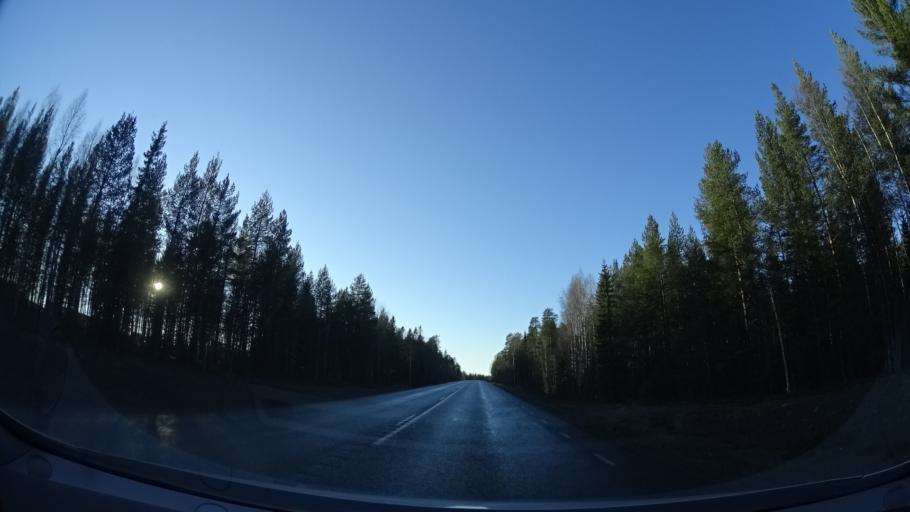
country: SE
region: Vaesterbotten
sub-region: Skelleftea Kommun
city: Boliden
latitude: 64.8764
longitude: 20.3691
